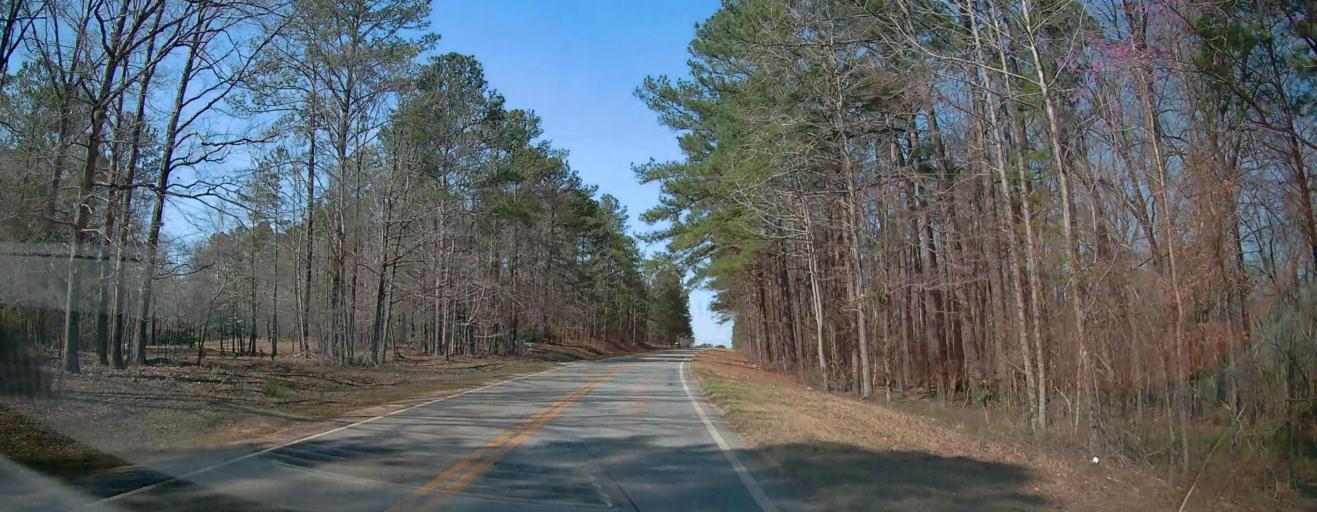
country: US
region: Georgia
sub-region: Jones County
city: Gray
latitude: 32.9281
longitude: -83.5337
